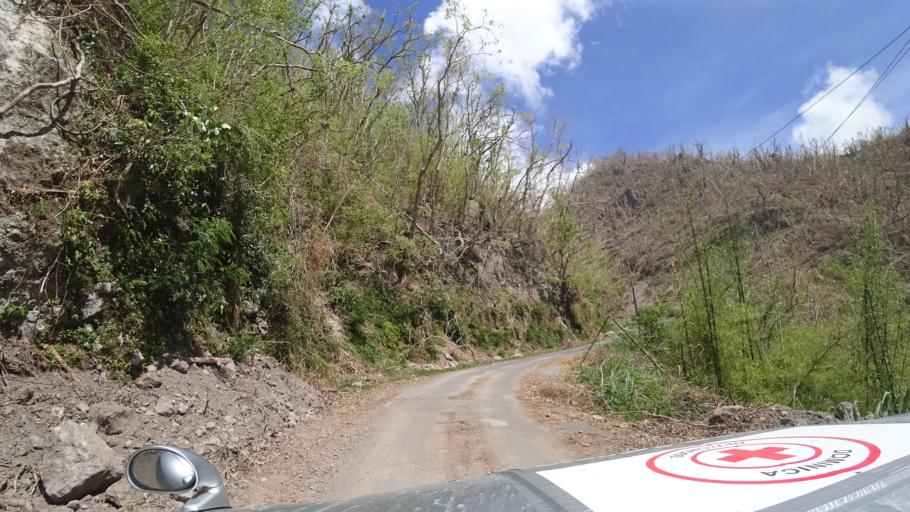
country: DM
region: Saint Mark
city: Soufriere
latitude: 15.2420
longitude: -61.3666
